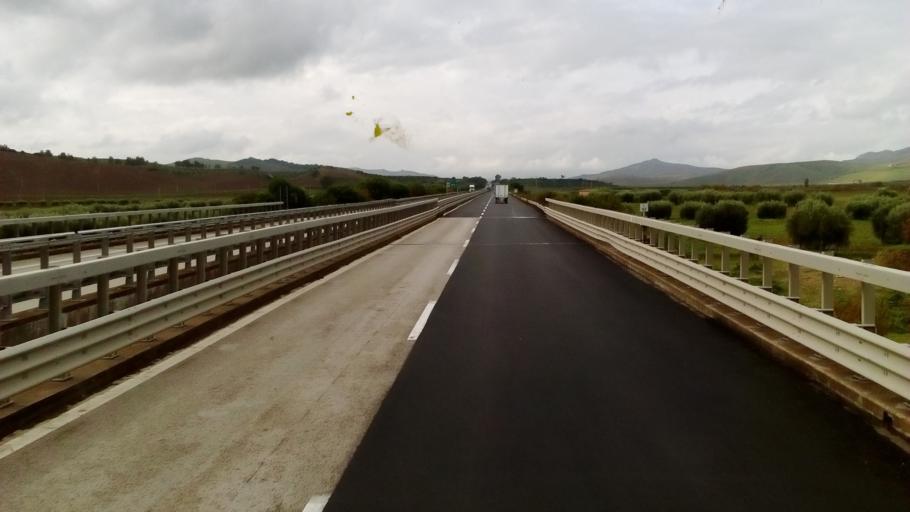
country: IT
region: Sicily
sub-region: Enna
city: Catenanuova
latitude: 37.5681
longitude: 14.6373
